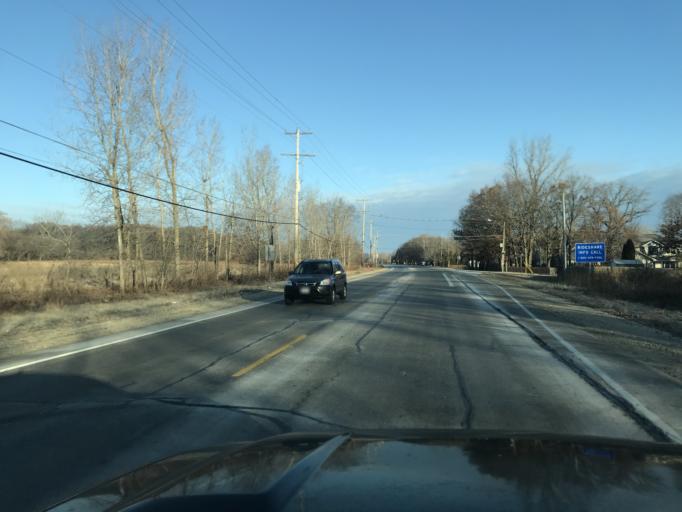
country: US
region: Illinois
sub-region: Lake County
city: Winthrop Harbor
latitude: 42.5244
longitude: -87.8243
